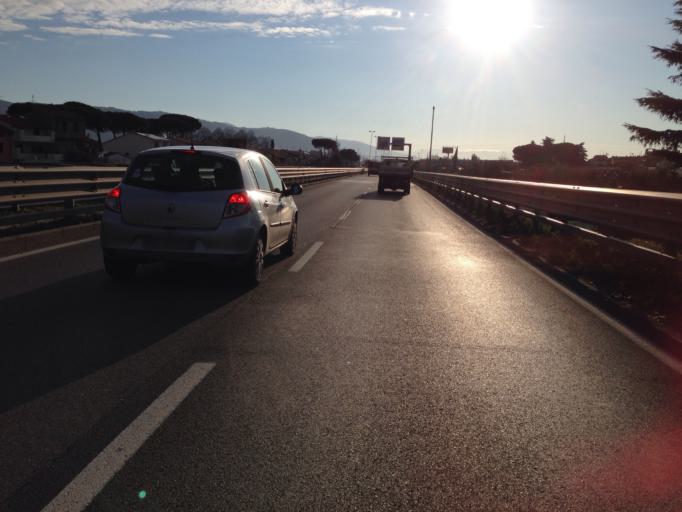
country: IT
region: Tuscany
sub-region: Provincia di Prato
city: Prato
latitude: 43.8801
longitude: 11.0578
